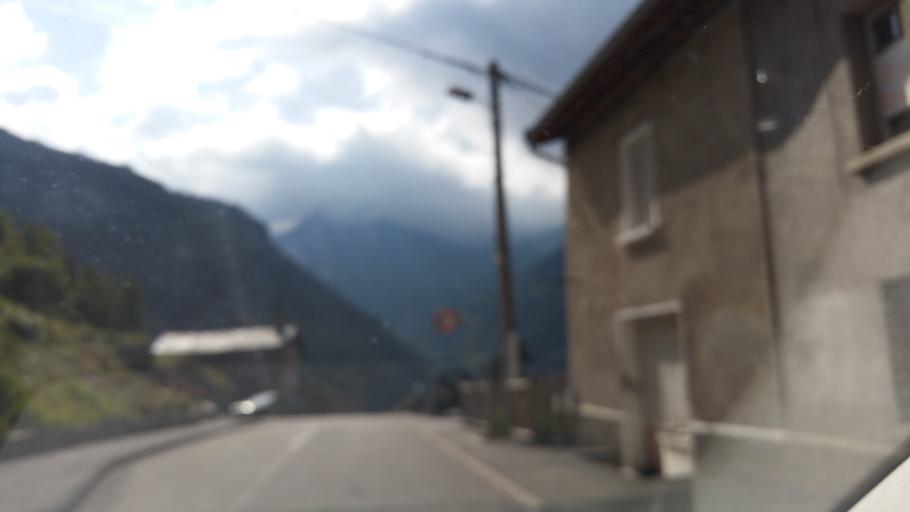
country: FR
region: Rhone-Alpes
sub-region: Departement de la Savoie
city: Modane
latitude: 45.2006
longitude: 6.6212
